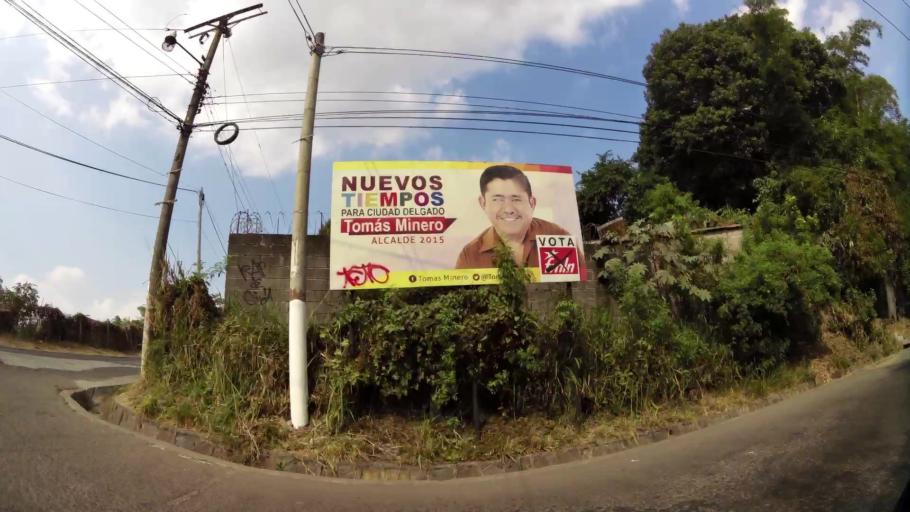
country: SV
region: San Salvador
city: Delgado
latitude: 13.7196
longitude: -89.1631
